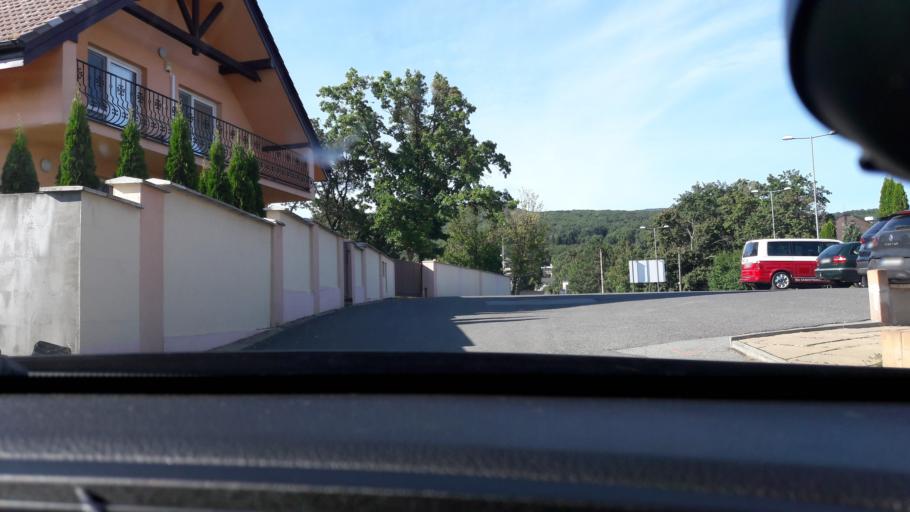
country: SK
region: Kosicky
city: Vinne
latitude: 48.8077
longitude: 22.0117
